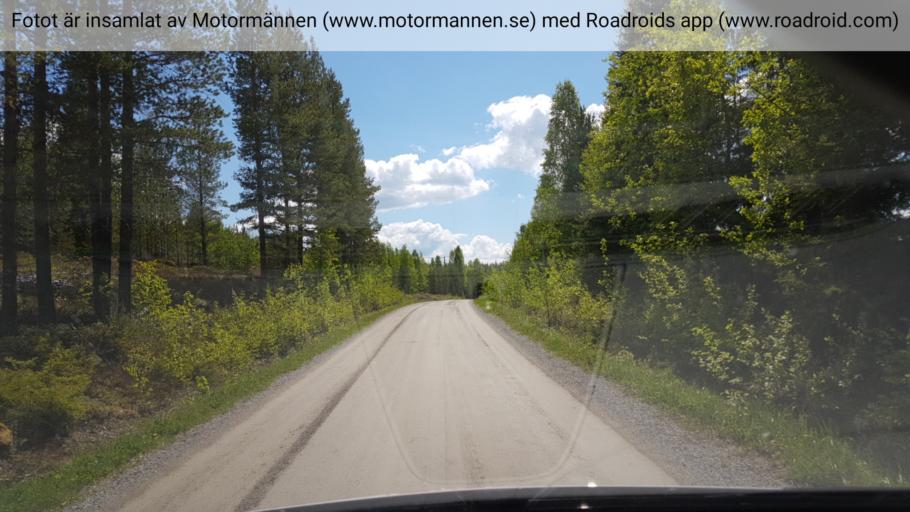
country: SE
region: Jaemtland
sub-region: OEstersunds Kommun
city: Brunflo
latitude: 63.0214
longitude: 15.0938
